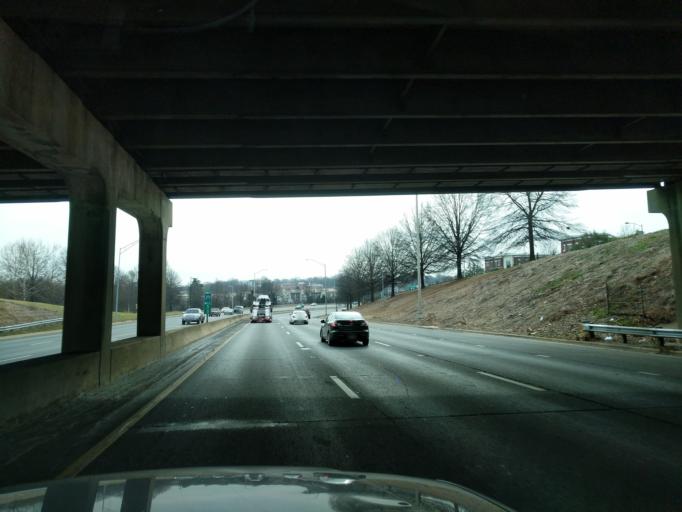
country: US
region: North Carolina
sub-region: Mecklenburg County
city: Charlotte
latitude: 35.2289
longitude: -80.8302
